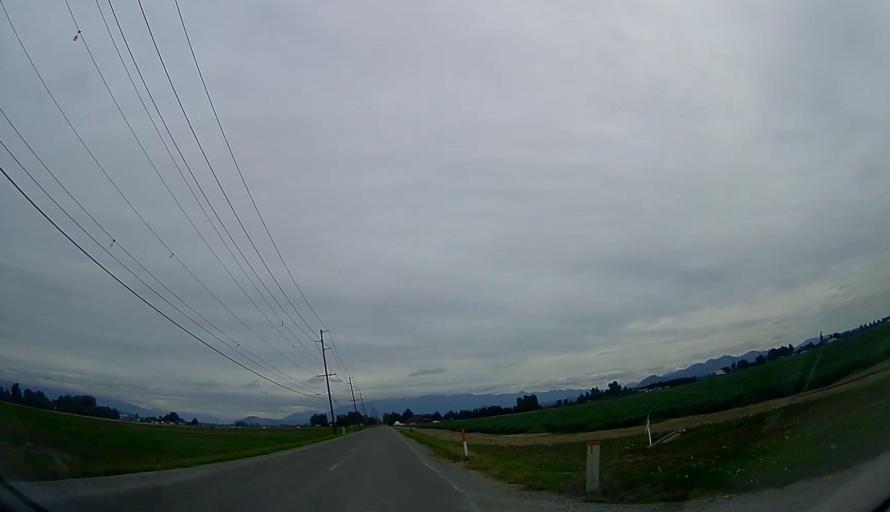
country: US
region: Washington
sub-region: Skagit County
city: Mount Vernon
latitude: 48.4427
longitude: -122.4325
